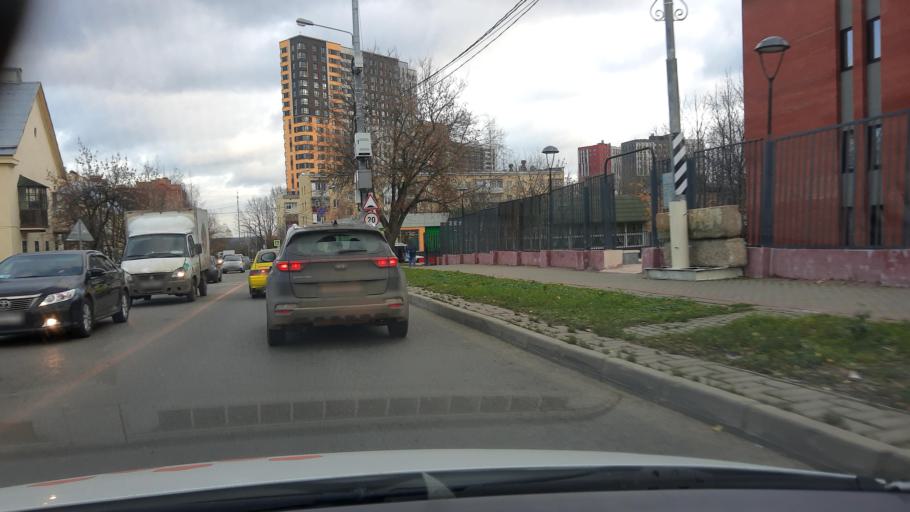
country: RU
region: Moskovskaya
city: Kommunarka
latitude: 55.5809
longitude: 37.4778
